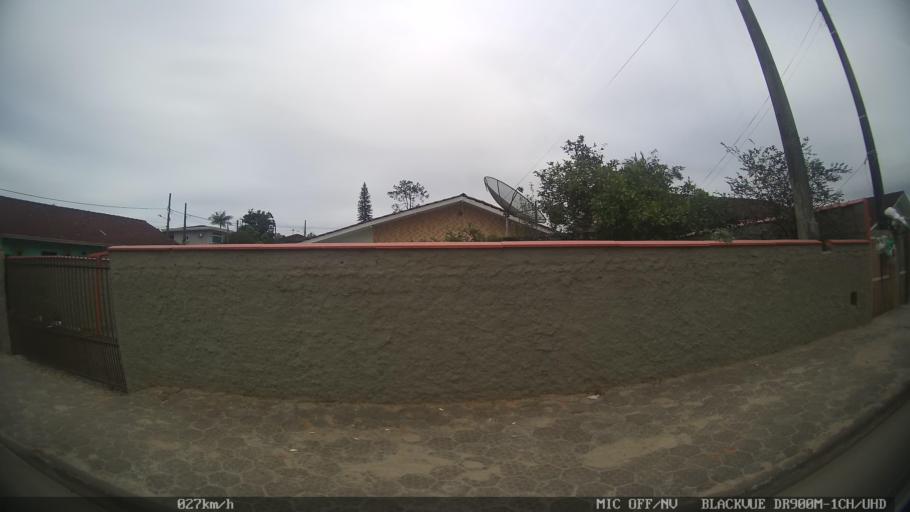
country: BR
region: Santa Catarina
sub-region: Joinville
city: Joinville
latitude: -26.3226
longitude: -48.9097
